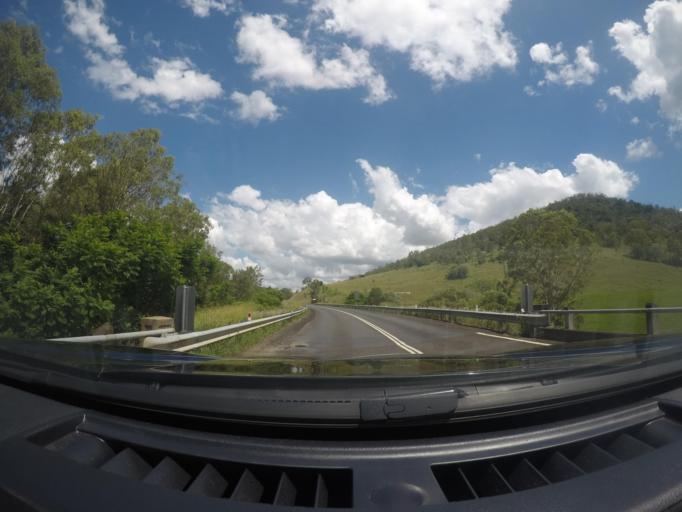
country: AU
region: Queensland
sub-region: Moreton Bay
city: Woodford
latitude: -27.1258
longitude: 152.5509
